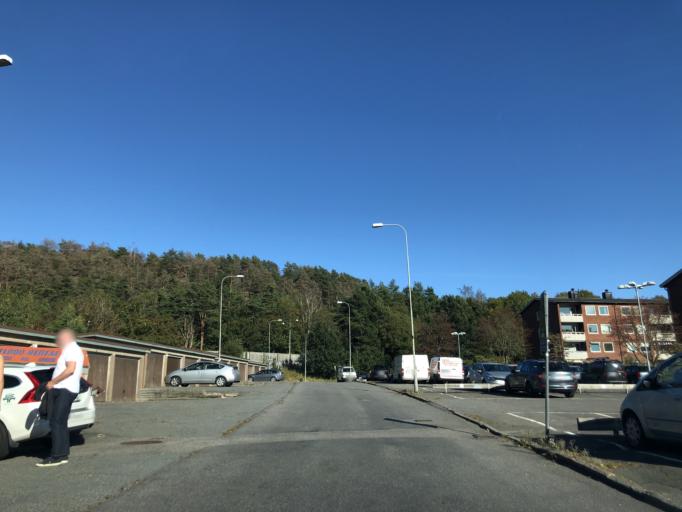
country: SE
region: Vaestra Goetaland
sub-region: Molndal
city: Moelndal
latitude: 57.6828
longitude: 12.0139
